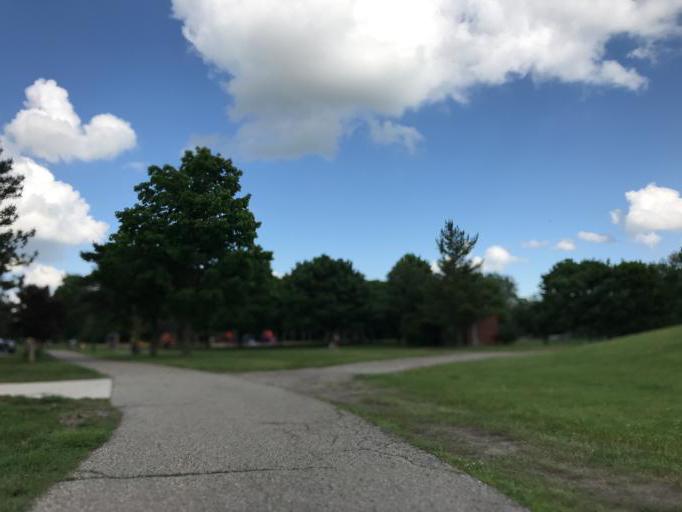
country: US
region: Michigan
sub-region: Oakland County
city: South Lyon
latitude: 42.4565
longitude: -83.6548
